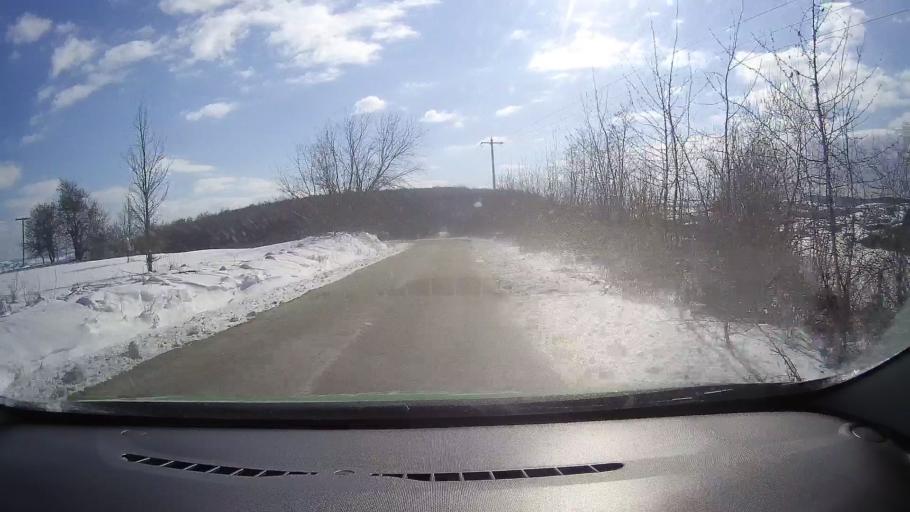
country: RO
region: Sibiu
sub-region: Comuna Altina
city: Altina
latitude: 45.9950
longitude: 24.4285
